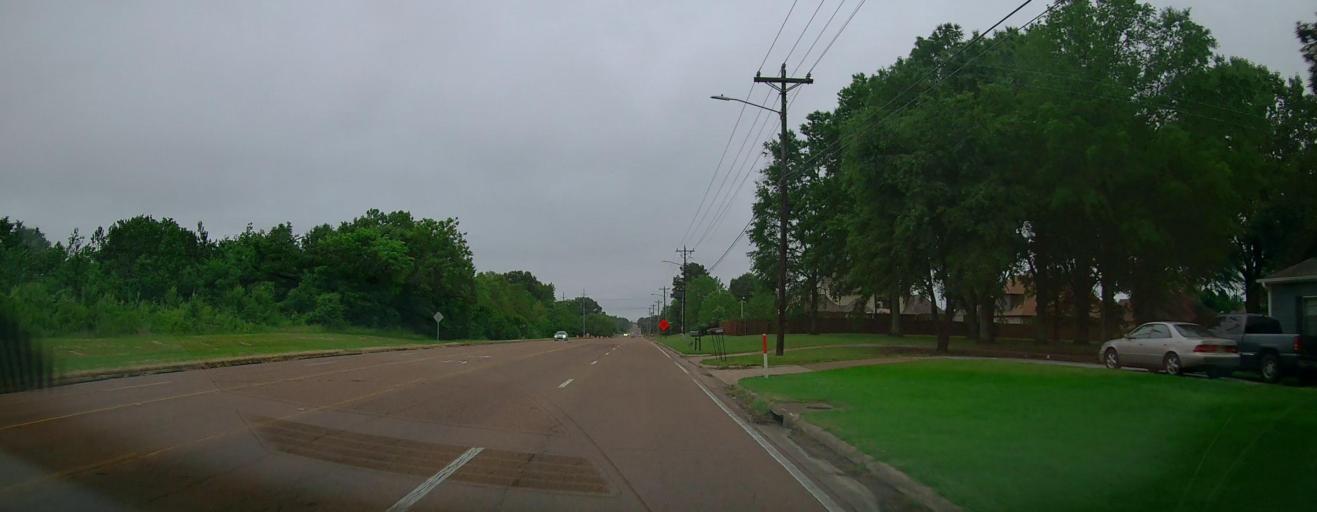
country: US
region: Mississippi
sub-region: De Soto County
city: Olive Branch
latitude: 34.9560
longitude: -89.7951
